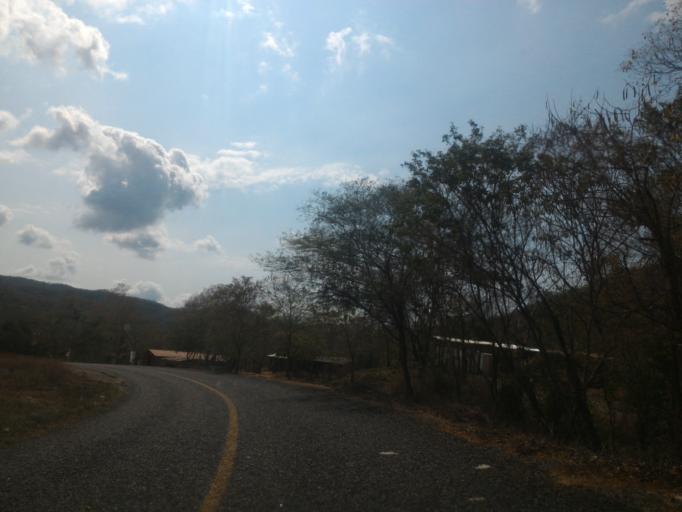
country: MX
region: Michoacan
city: Coahuayana Viejo
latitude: 18.4587
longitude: -103.5412
